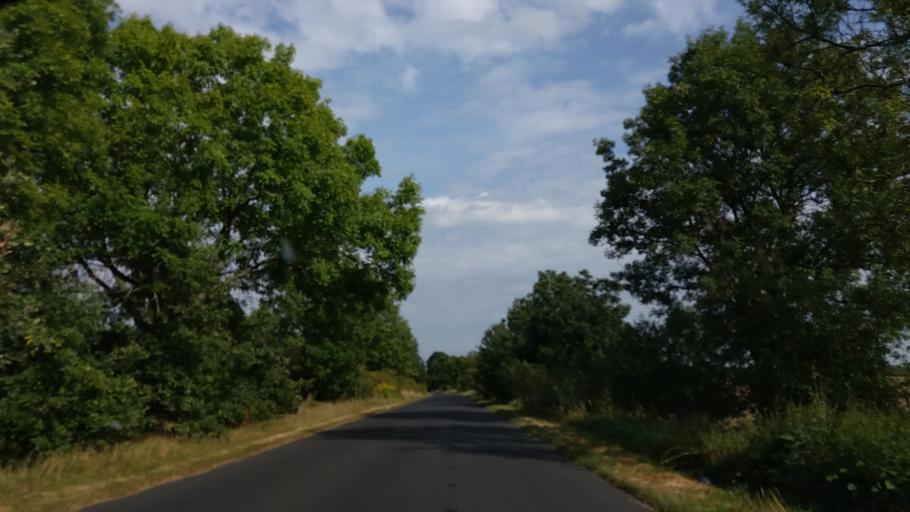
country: PL
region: West Pomeranian Voivodeship
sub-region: Powiat stargardzki
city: Suchan
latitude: 53.2236
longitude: 15.2918
